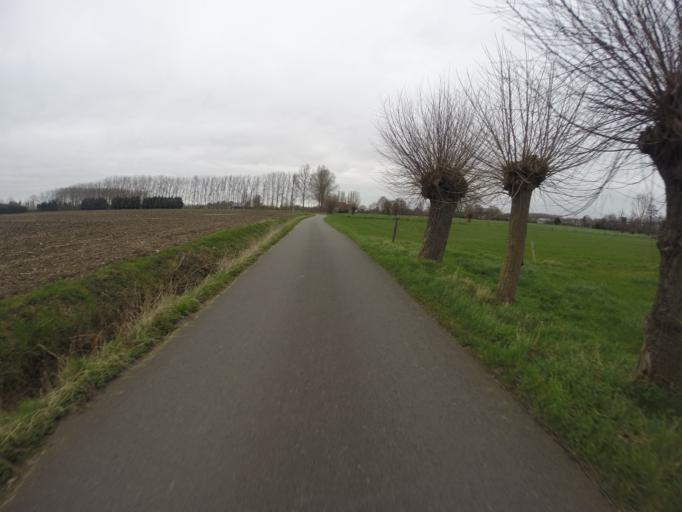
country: BE
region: Flanders
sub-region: Provincie Oost-Vlaanderen
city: Aalter
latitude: 51.1154
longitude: 3.4410
